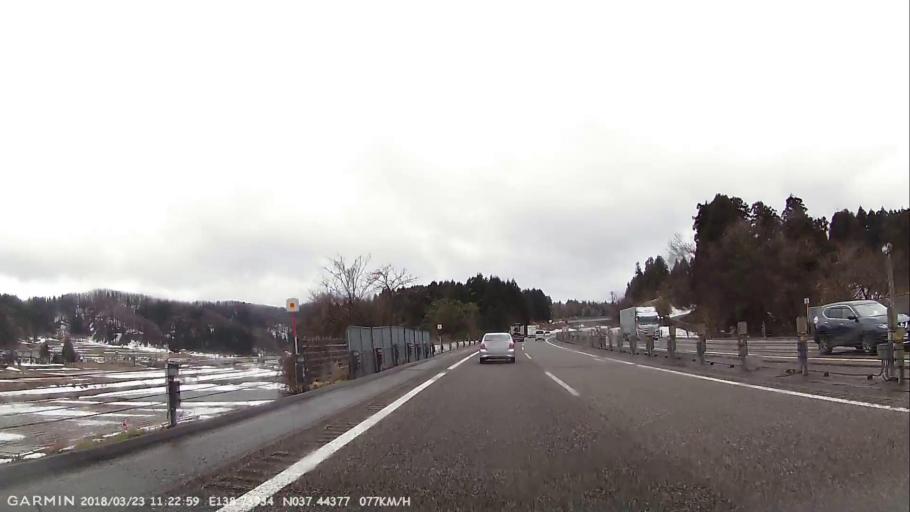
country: JP
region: Niigata
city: Nagaoka
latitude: 37.4436
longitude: 138.7392
